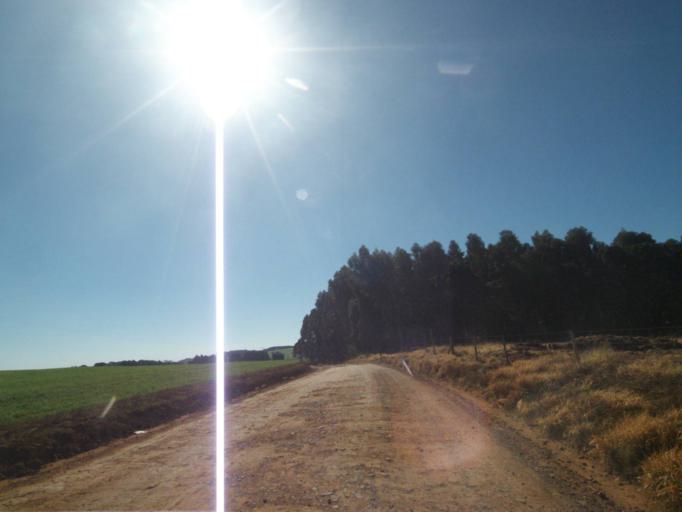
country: BR
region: Parana
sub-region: Tibagi
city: Tibagi
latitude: -24.6138
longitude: -50.6057
